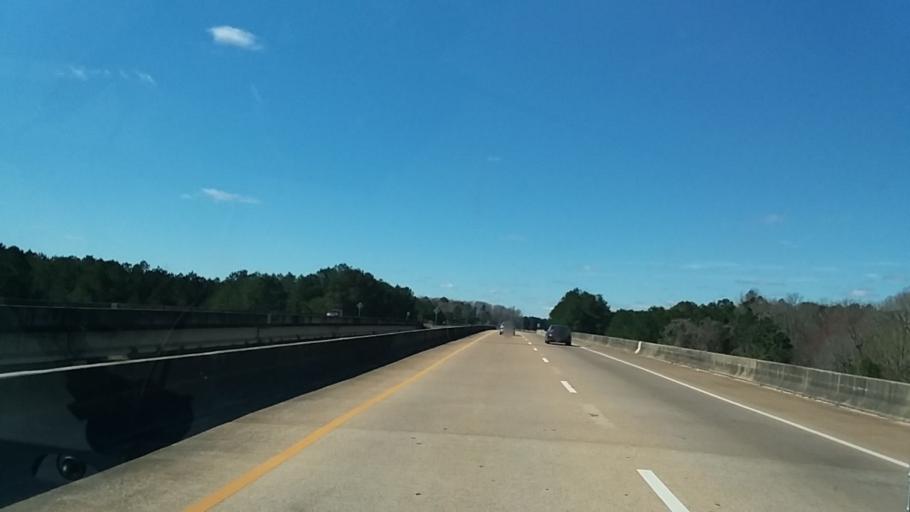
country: US
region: Mississippi
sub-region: Alcorn County
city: Farmington
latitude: 34.8805
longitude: -88.4450
